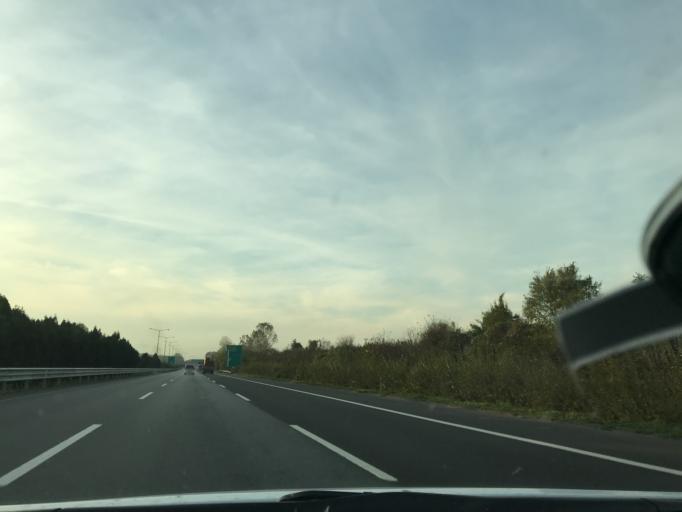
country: TR
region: Duzce
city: Cilimli
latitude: 40.8271
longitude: 31.0529
